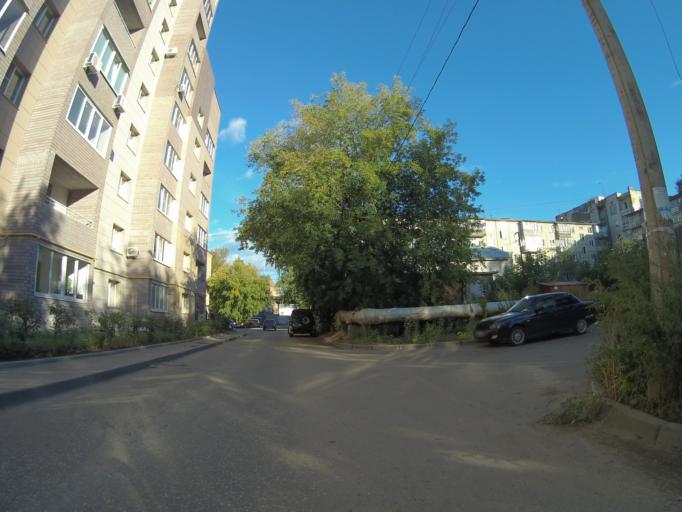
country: RU
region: Vladimir
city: Vladimir
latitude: 56.1519
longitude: 40.3778
